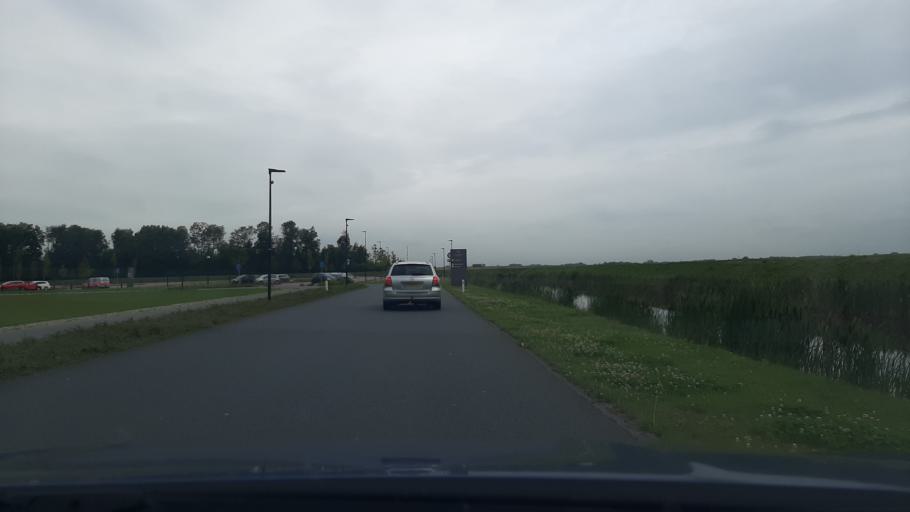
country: NL
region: Groningen
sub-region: Gemeente  Oldambt
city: Winschoten
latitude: 53.1837
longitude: 6.9597
